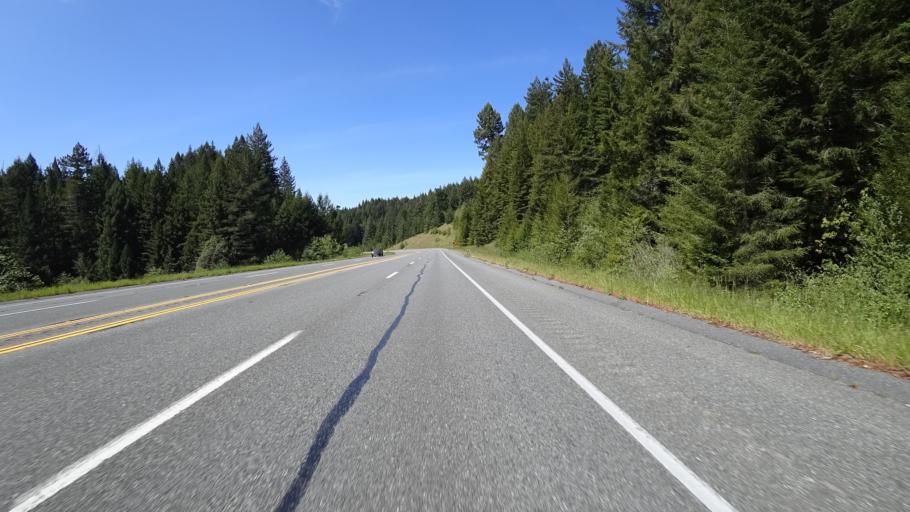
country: US
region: California
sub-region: Humboldt County
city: Westhaven-Moonstone
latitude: 41.3586
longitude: -124.0092
